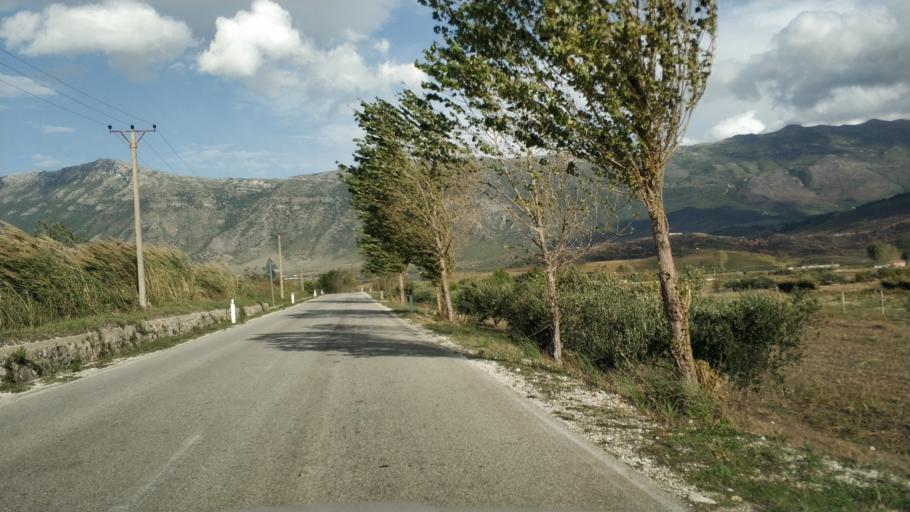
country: AL
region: Vlore
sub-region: Rrethi i Vlores
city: Orikum
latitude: 40.3119
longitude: 19.4816
